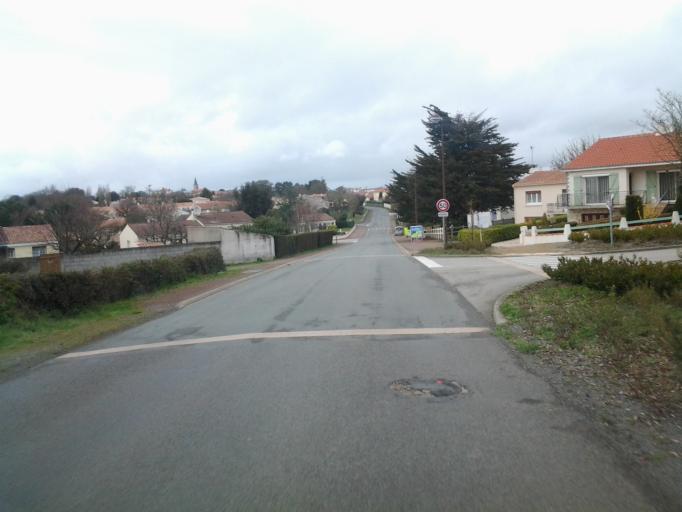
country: FR
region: Pays de la Loire
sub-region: Departement de la Vendee
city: Avrille
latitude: 46.4641
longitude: -1.4890
